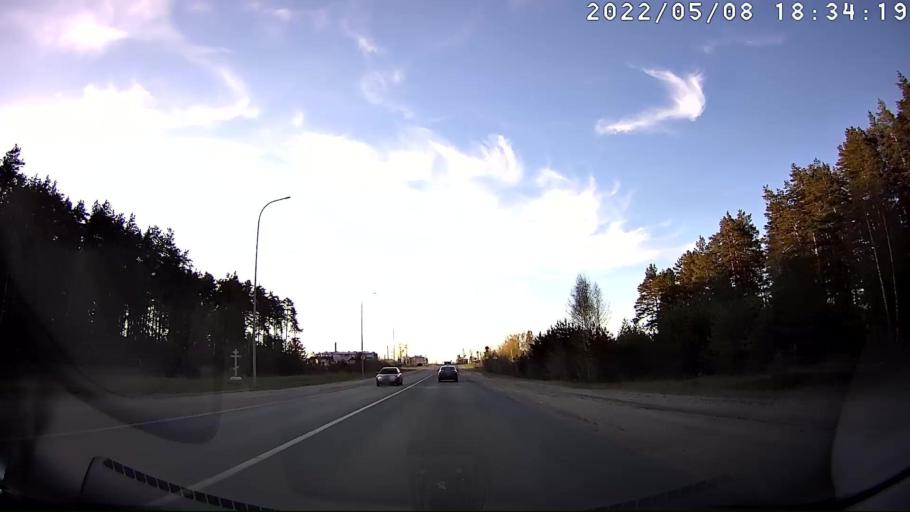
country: RU
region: Mariy-El
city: Volzhsk
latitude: 55.8992
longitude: 48.3563
